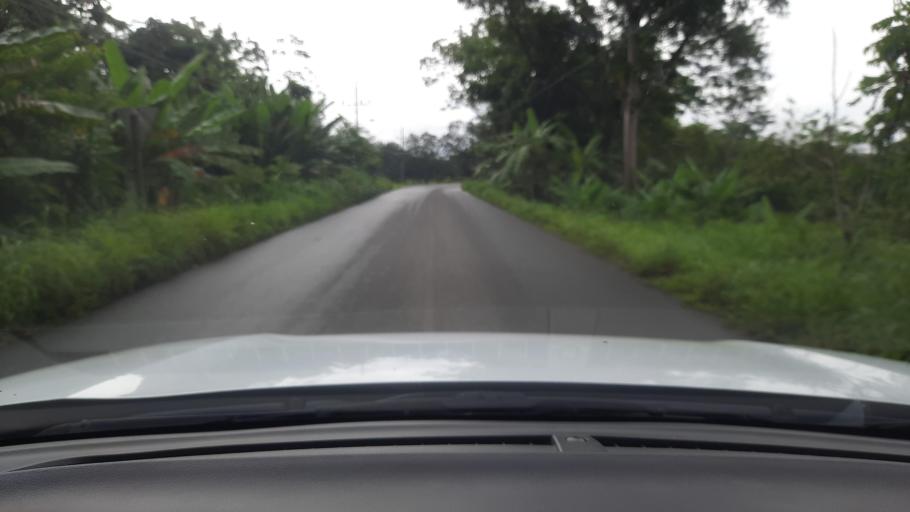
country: CR
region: Alajuela
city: San Jose
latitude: 10.9279
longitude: -85.0940
